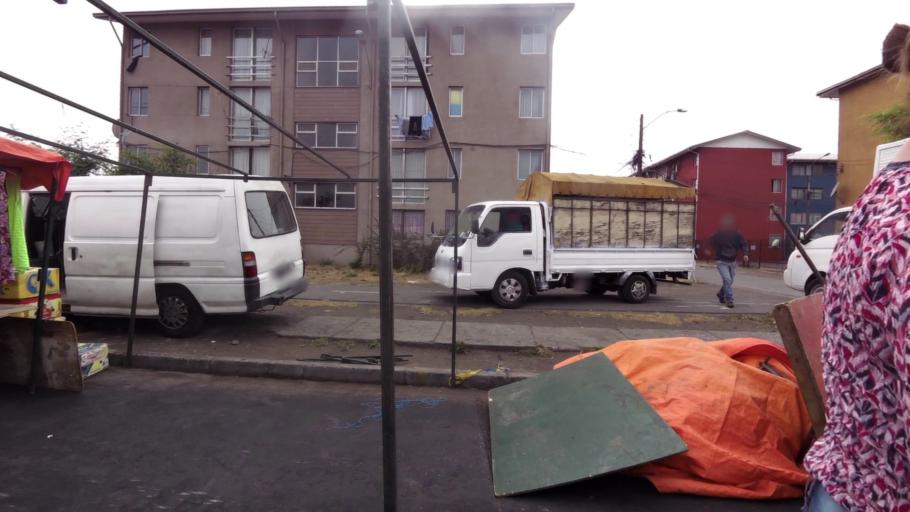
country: CL
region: Biobio
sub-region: Provincia de Concepcion
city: Concepcion
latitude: -36.7920
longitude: -73.0943
